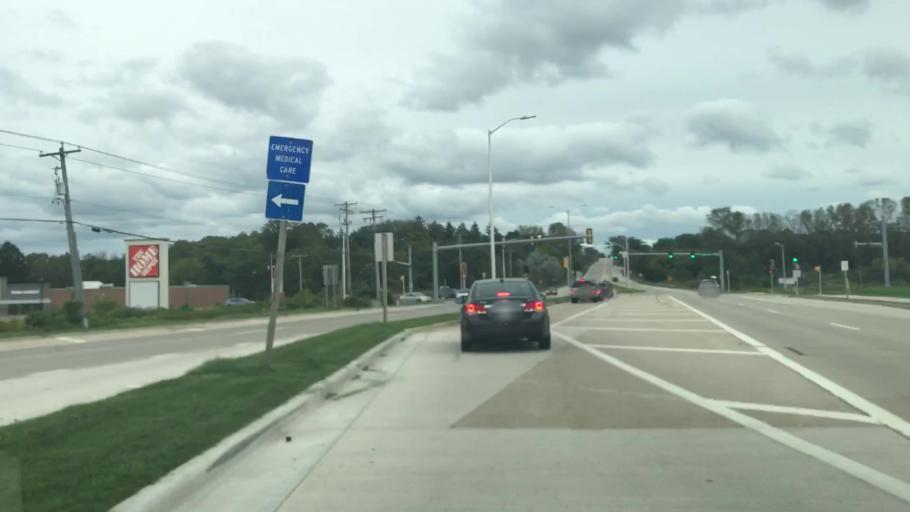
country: US
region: Wisconsin
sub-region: Waukesha County
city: Mukwonago
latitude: 42.8494
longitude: -88.3195
